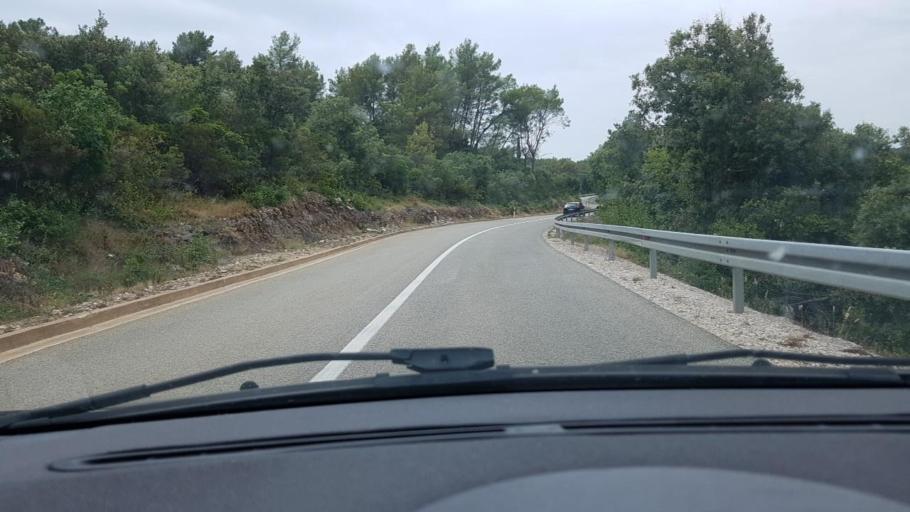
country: HR
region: Dubrovacko-Neretvanska
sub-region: Grad Korcula
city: Zrnovo
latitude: 42.9384
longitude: 17.0898
